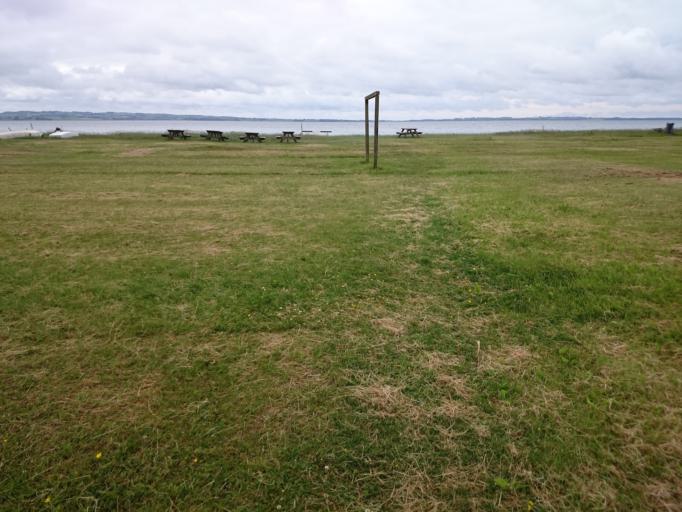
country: DK
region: Central Jutland
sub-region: Syddjurs Kommune
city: Ronde
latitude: 56.2934
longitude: 10.4204
